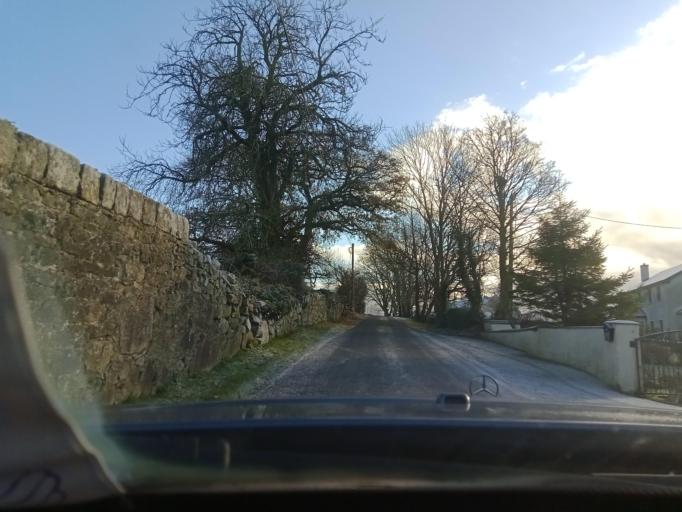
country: IE
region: Leinster
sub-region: Kilkenny
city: Graiguenamanagh
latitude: 52.5999
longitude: -6.9857
